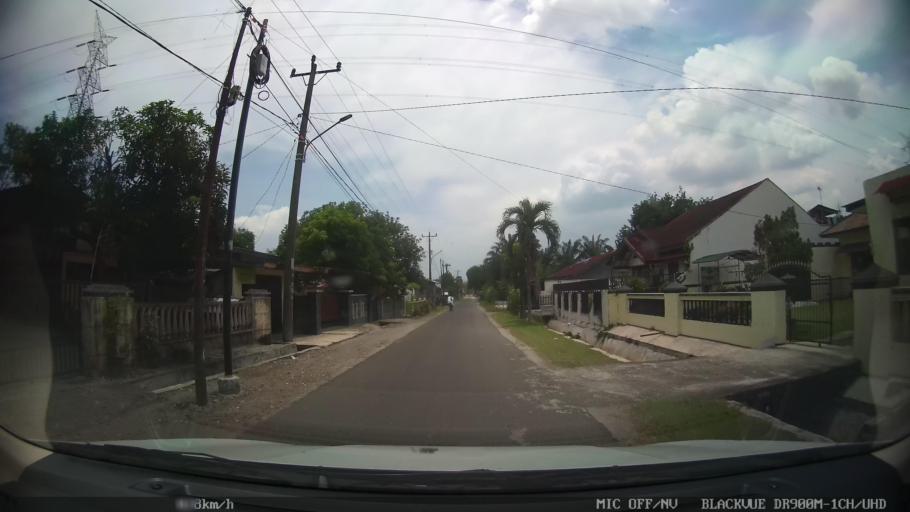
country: ID
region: North Sumatra
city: Binjai
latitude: 3.6208
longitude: 98.5042
